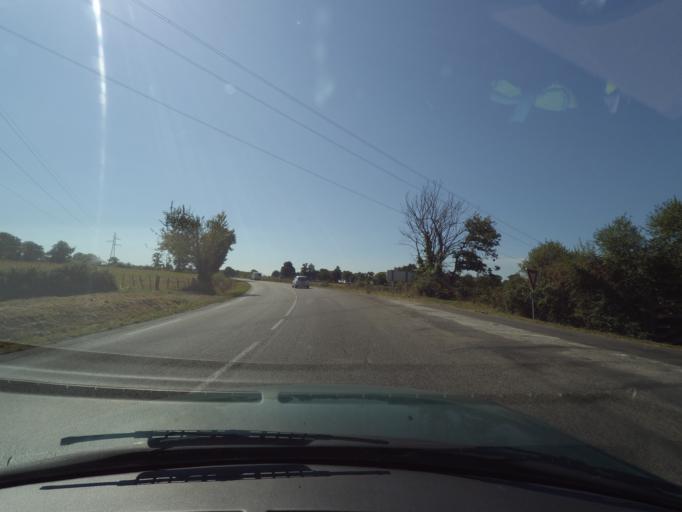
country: FR
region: Limousin
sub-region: Departement de la Haute-Vienne
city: Bellac
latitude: 46.0910
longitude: 1.0796
